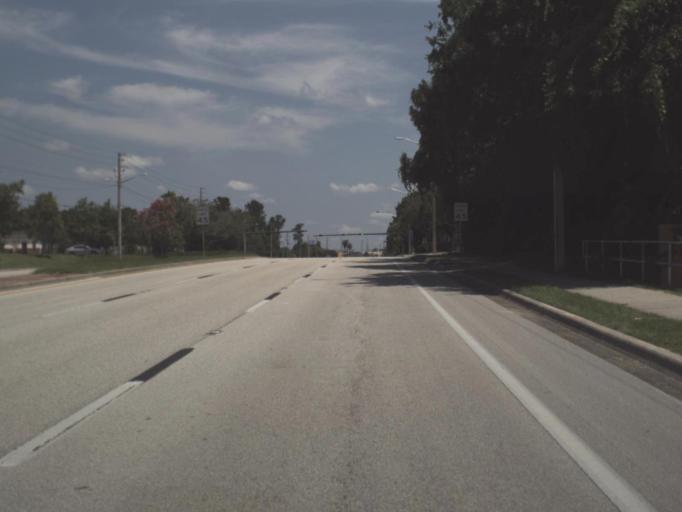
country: US
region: Florida
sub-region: Alachua County
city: Gainesville
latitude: 29.6161
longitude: -82.3721
